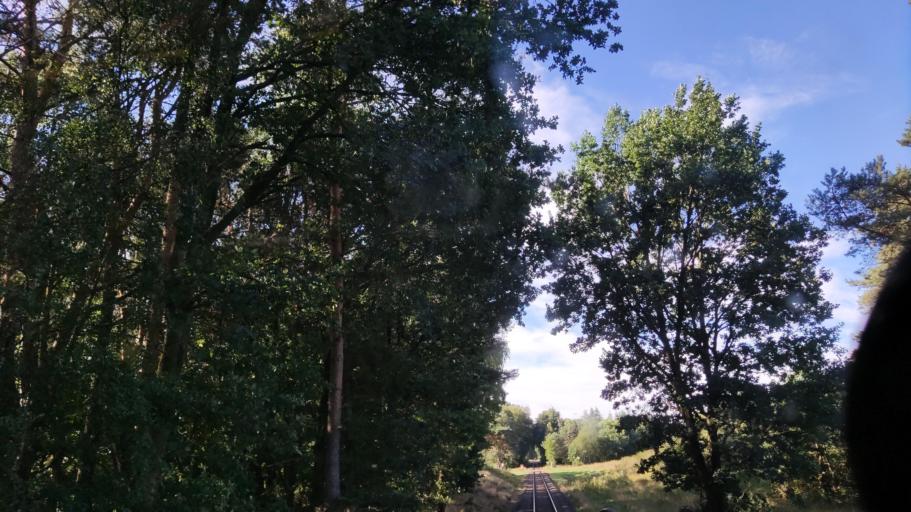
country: DE
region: Lower Saxony
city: Bispingen
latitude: 53.0414
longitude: 9.9394
